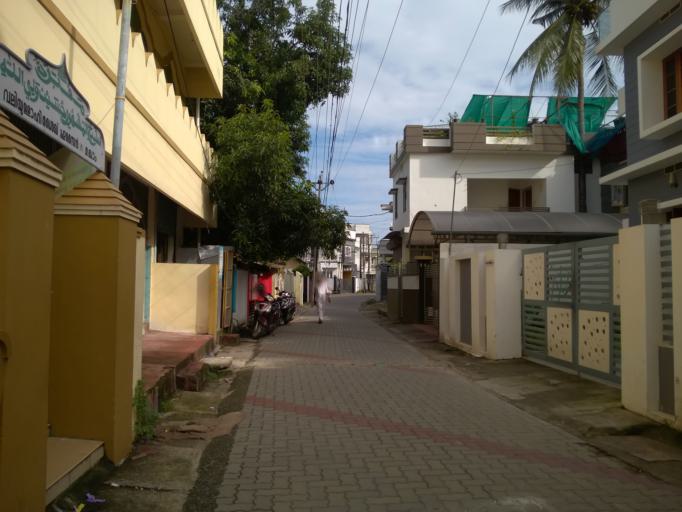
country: IN
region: Kerala
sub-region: Ernakulam
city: Cochin
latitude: 9.9525
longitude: 76.2596
